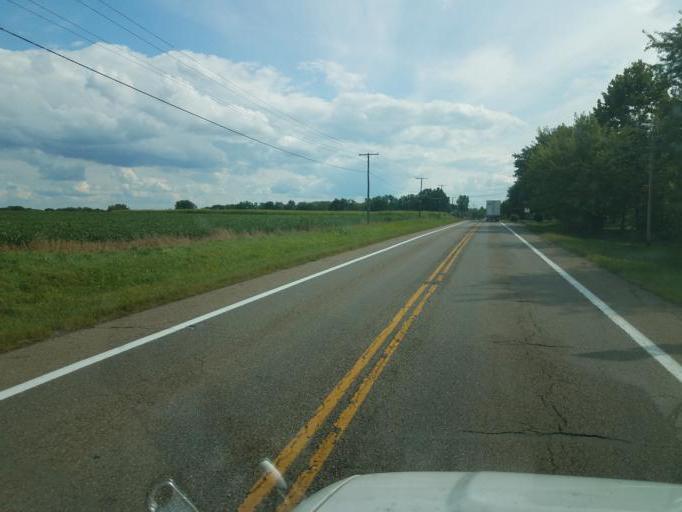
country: US
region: Ohio
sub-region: Stark County
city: Louisville
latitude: 40.8763
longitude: -81.2576
